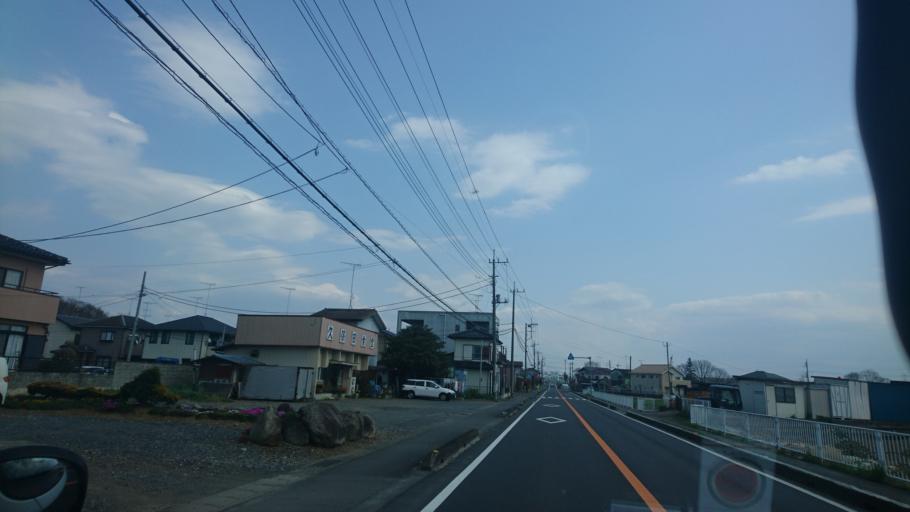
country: JP
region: Ibaraki
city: Yuki
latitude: 36.2809
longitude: 139.9013
